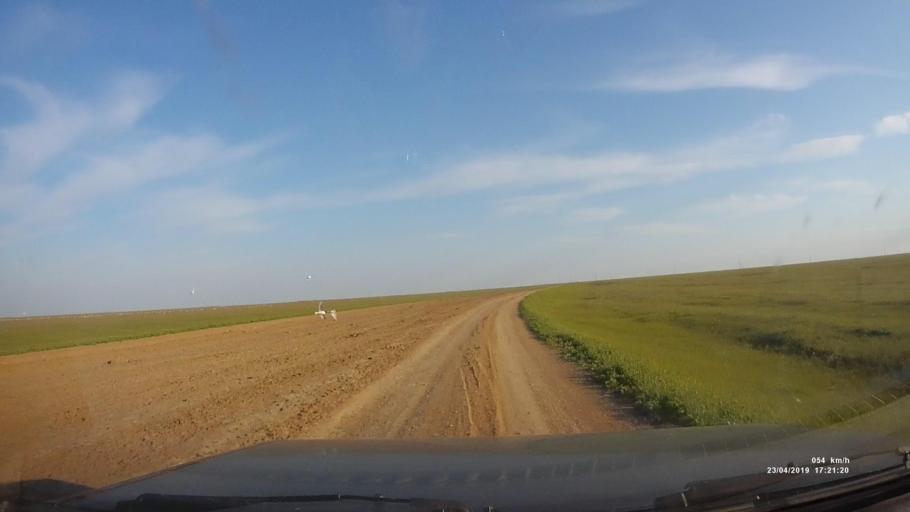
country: RU
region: Kalmykiya
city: Priyutnoye
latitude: 46.1769
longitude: 43.5050
